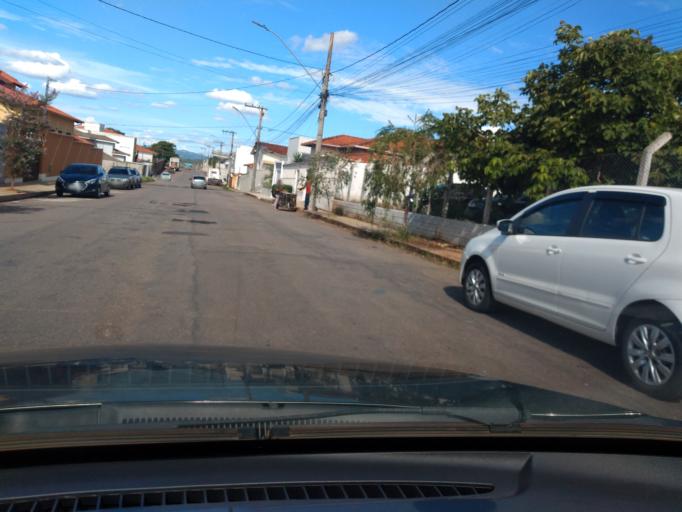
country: BR
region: Minas Gerais
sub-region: Tres Coracoes
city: Tres Coracoes
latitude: -21.6882
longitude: -45.2648
